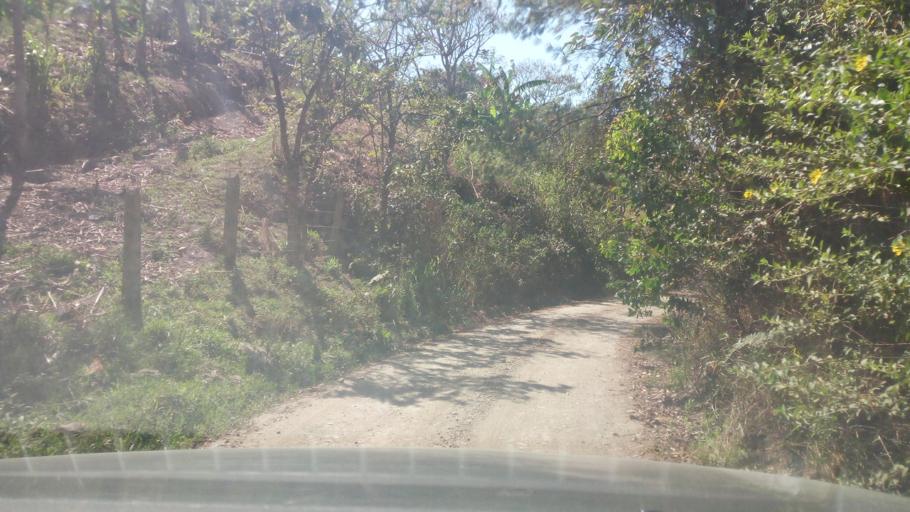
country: CO
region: Boyaca
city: Somondoco
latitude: 4.9920
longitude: -73.4144
